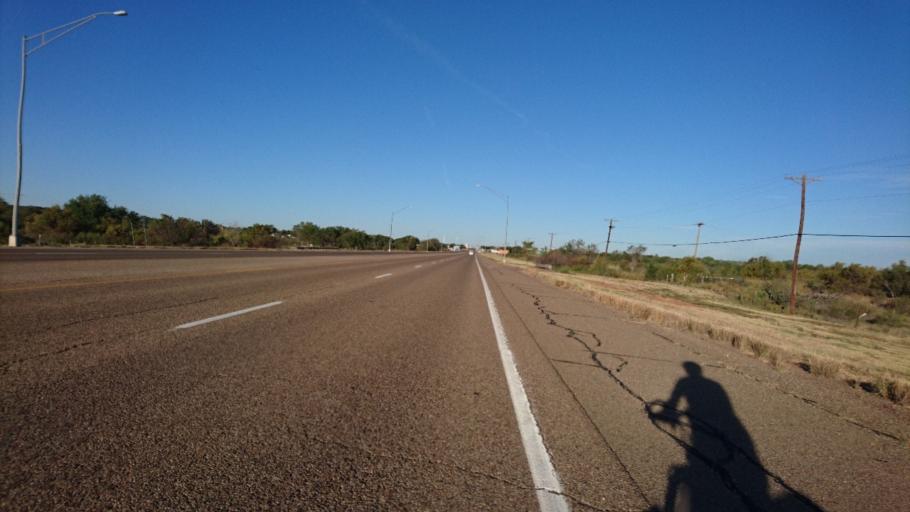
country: US
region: New Mexico
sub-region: Quay County
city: Tucumcari
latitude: 35.1720
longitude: -103.6945
